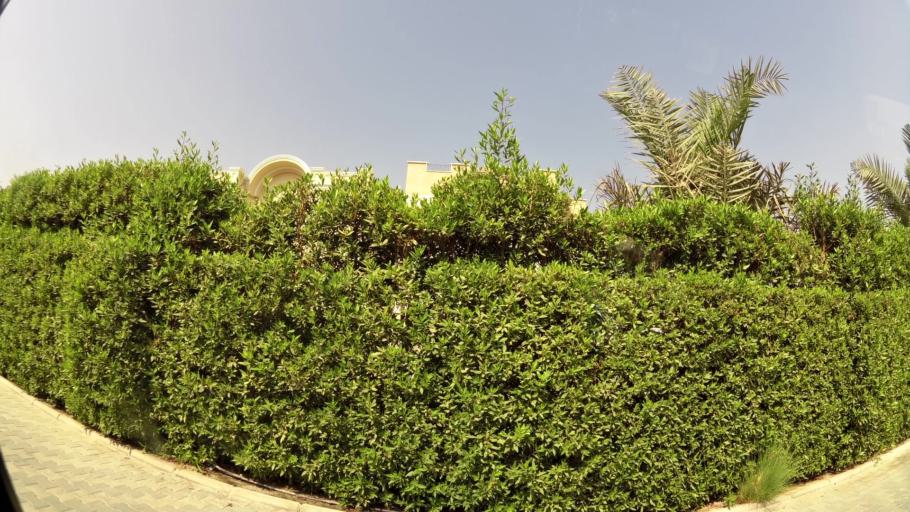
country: KW
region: Al Asimah
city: Ad Dasmah
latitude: 29.3563
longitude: 47.9984
